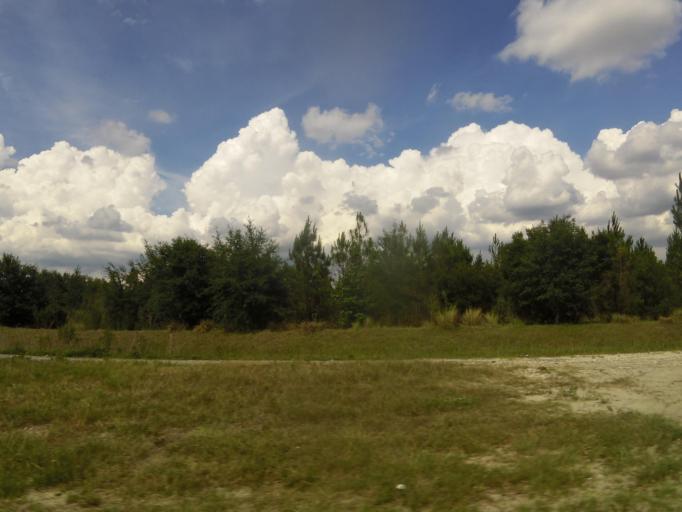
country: US
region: Florida
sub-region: Baker County
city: Macclenny
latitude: 30.2152
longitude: -82.0692
